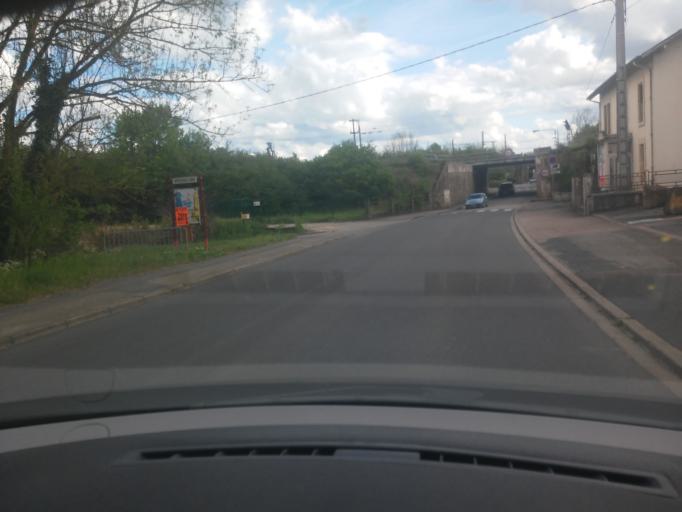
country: FR
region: Lorraine
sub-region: Departement de Meurthe-et-Moselle
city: Labry
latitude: 49.1673
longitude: 5.8817
